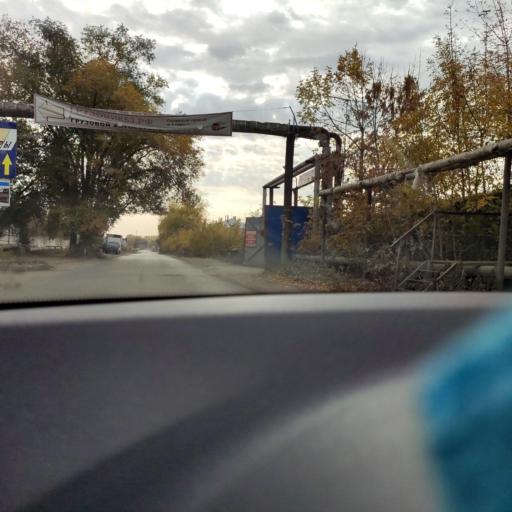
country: RU
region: Samara
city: Samara
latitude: 53.1950
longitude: 50.2611
